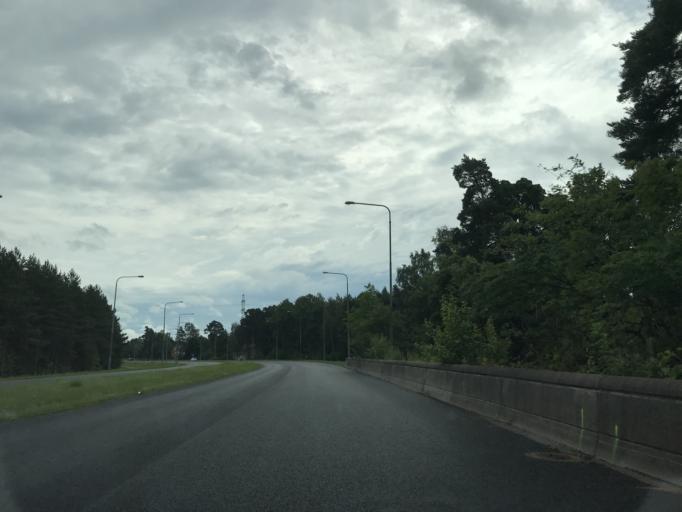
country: FI
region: Varsinais-Suomi
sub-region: Turku
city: Kaarina
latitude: 60.4224
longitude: 22.3161
